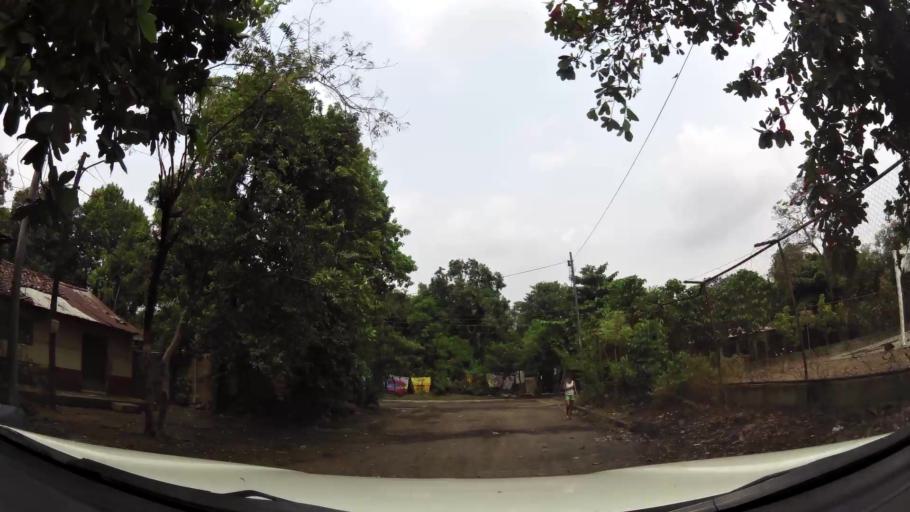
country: NI
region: Chinandega
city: Chinandega
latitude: 12.6504
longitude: -87.1226
